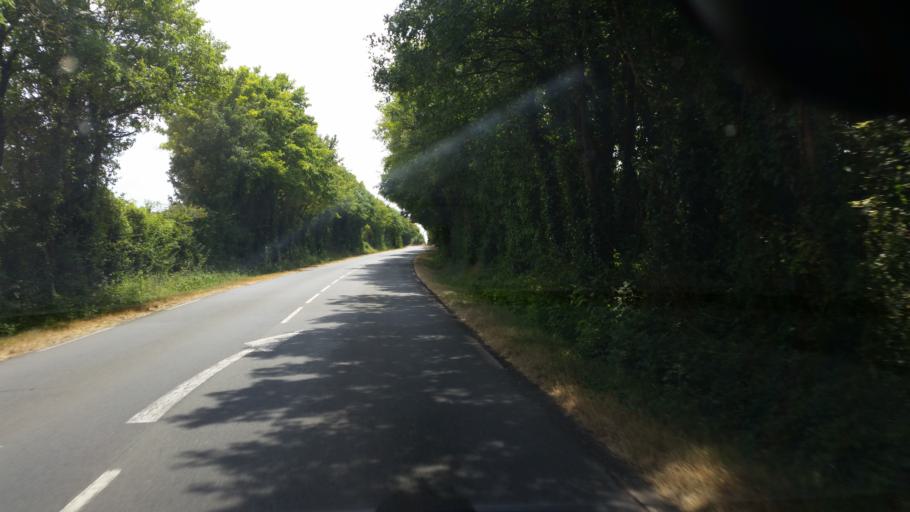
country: FR
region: Poitou-Charentes
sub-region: Departement de la Charente-Maritime
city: Surgeres
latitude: 46.1227
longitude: -0.7682
